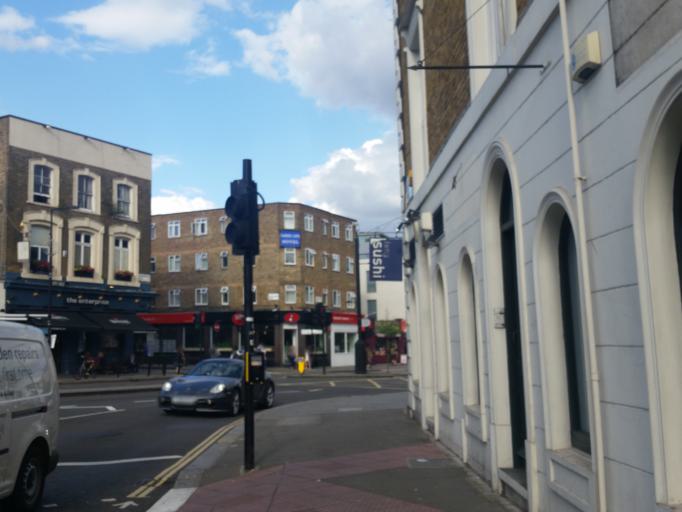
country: GB
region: England
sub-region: Greater London
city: Camden Town
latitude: 51.5439
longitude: -0.1532
